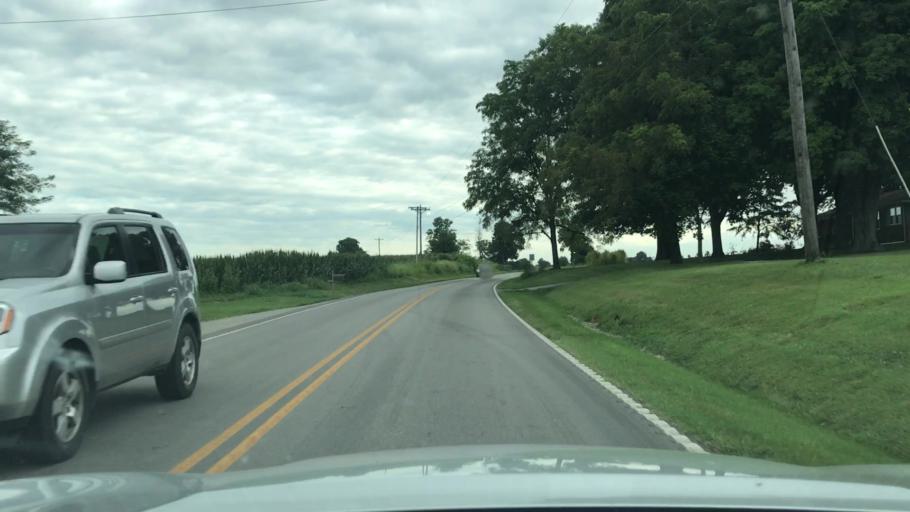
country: US
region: Kentucky
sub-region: Todd County
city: Guthrie
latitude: 36.7030
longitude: -87.1973
